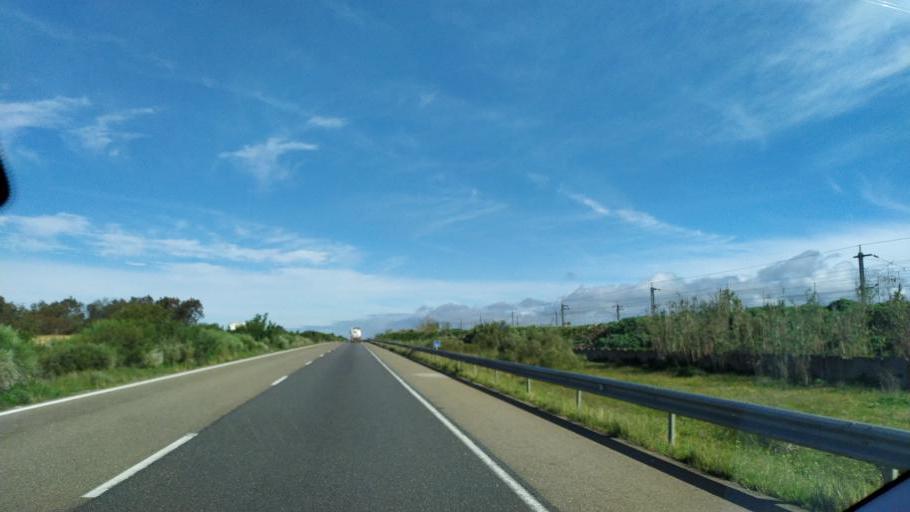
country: MA
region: Gharb-Chrarda-Beni Hssen
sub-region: Kenitra Province
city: Lalla Mimouna
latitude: 34.6956
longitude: -6.3812
